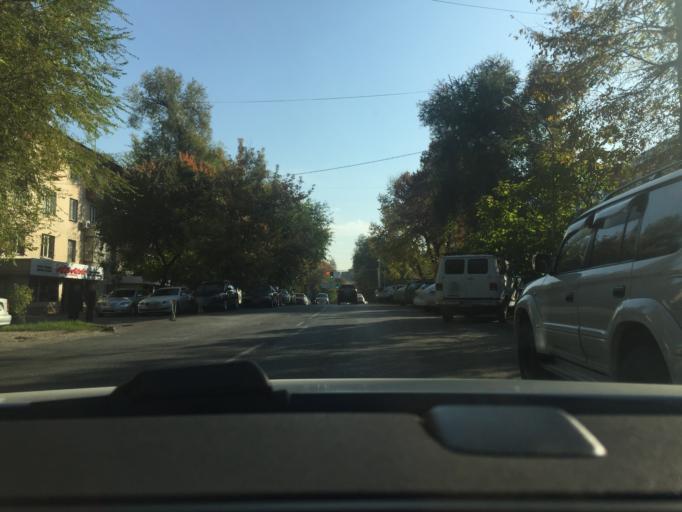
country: KZ
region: Almaty Qalasy
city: Almaty
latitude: 43.2465
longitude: 76.9249
